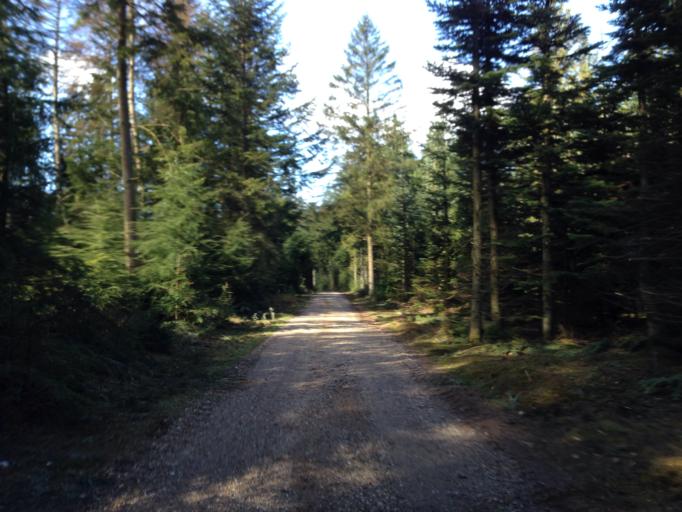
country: DK
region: Central Jutland
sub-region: Holstebro Kommune
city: Ulfborg
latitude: 56.2513
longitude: 8.4524
